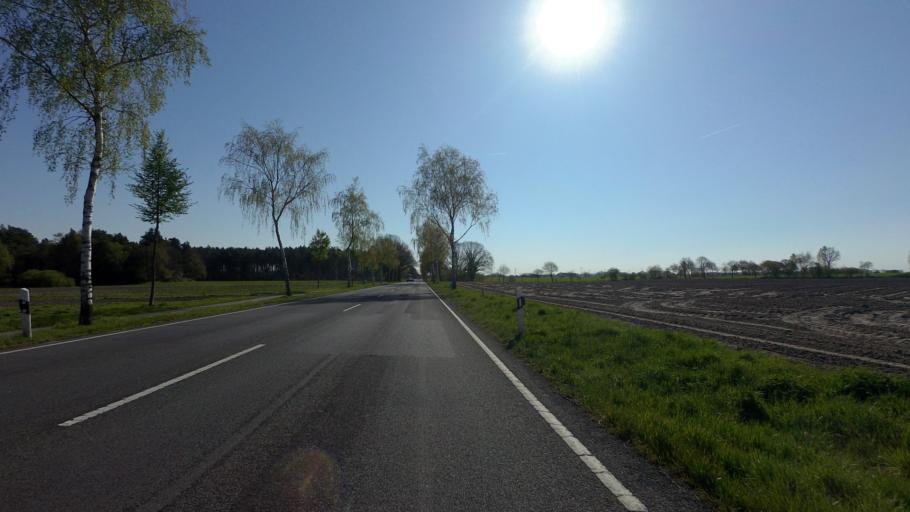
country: DE
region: Lower Saxony
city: Steimbke
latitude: 52.6578
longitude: 9.3663
